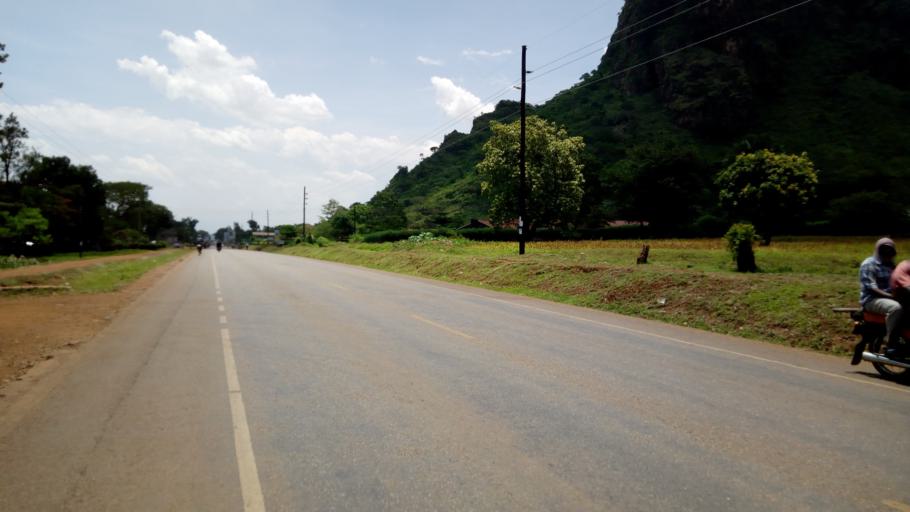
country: UG
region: Eastern Region
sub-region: Tororo District
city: Tororo
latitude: 0.6820
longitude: 34.1782
